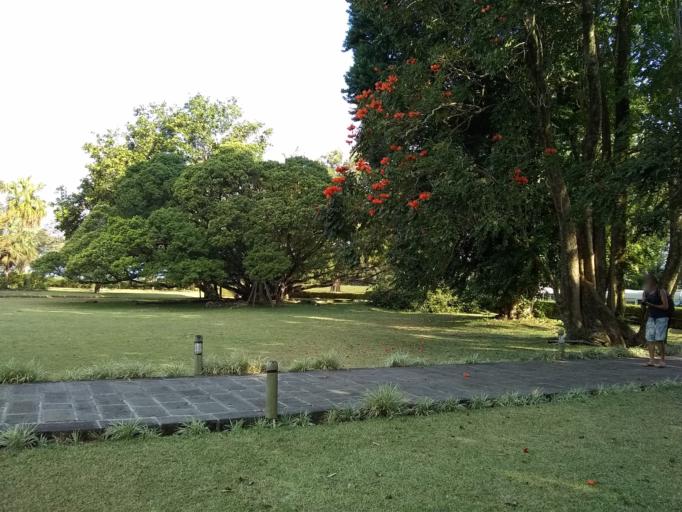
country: MU
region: Savanne
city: Saint Aubin
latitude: -20.5019
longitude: 57.5444
